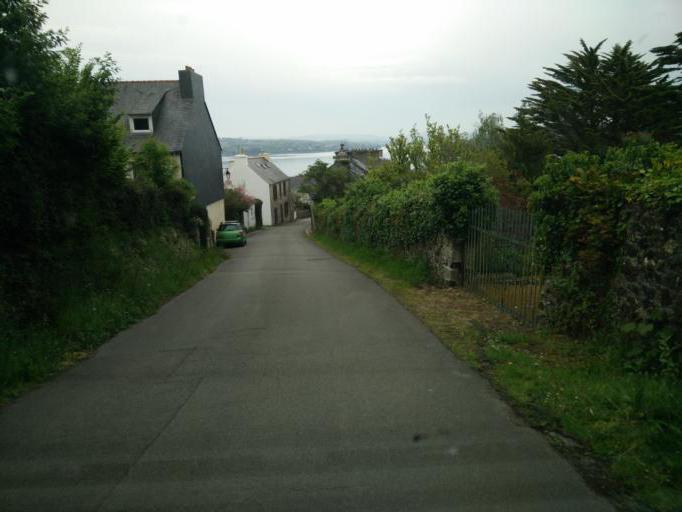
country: FR
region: Brittany
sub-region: Departement du Finistere
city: Logonna-Daoulas
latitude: 48.2913
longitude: -4.2693
